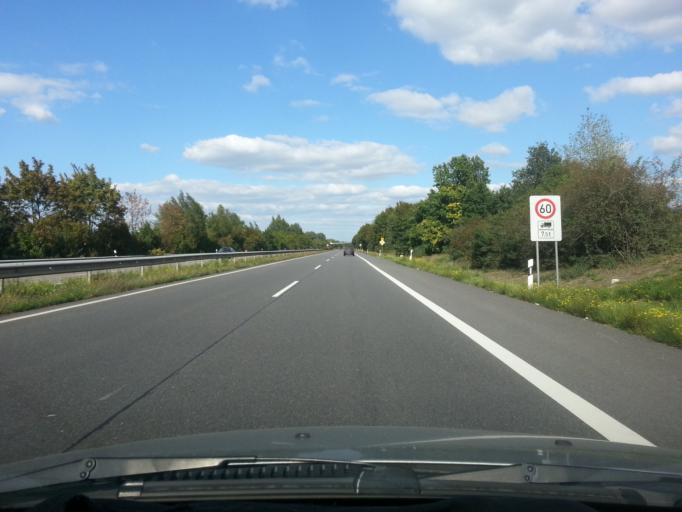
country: DE
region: Baden-Wuerttemberg
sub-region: Karlsruhe Region
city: Neulussheim
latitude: 49.3101
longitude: 8.5342
